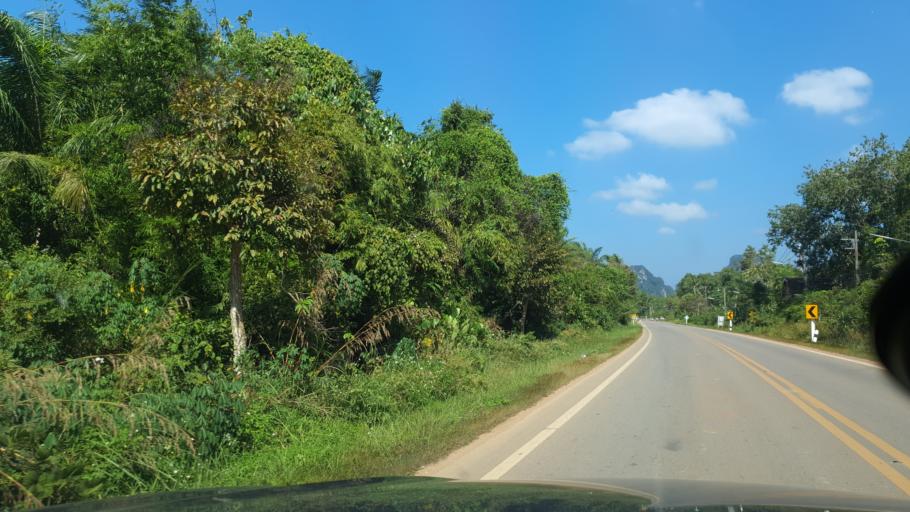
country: TH
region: Phangnga
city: Ban Ao Nang
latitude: 8.0501
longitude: 98.8594
